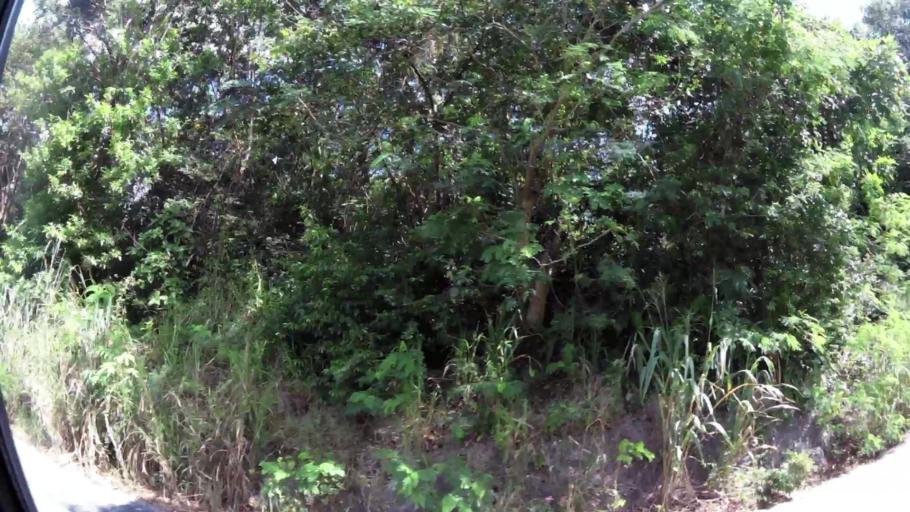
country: BB
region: Saint James
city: Holetown
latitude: 13.2156
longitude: -59.6158
